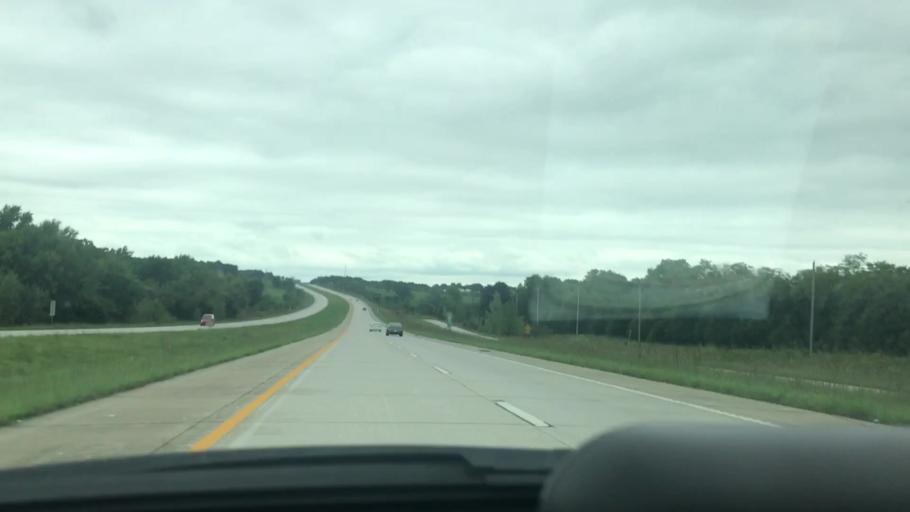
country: US
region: Missouri
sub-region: Dallas County
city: Buffalo
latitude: 37.5257
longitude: -93.1376
